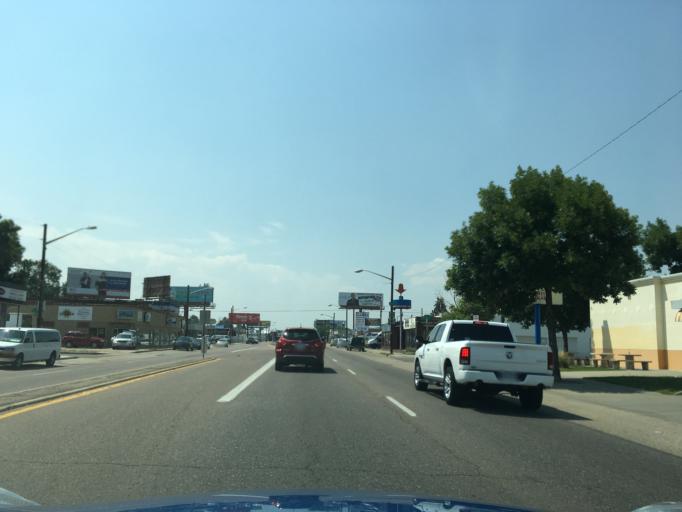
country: US
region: Colorado
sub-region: Arapahoe County
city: Glendale
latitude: 39.7402
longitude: -104.8991
